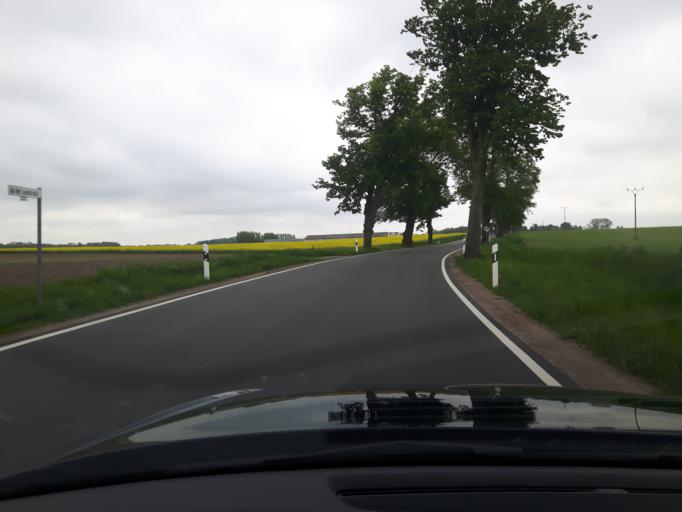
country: DE
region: Mecklenburg-Vorpommern
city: Gnoien
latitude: 54.0189
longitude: 12.6547
